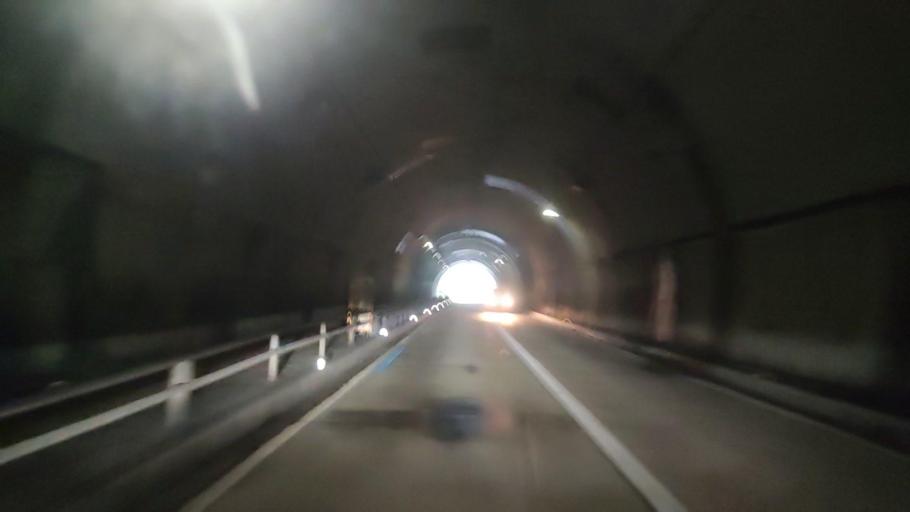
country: JP
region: Wakayama
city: Shingu
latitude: 33.8177
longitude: 135.7592
